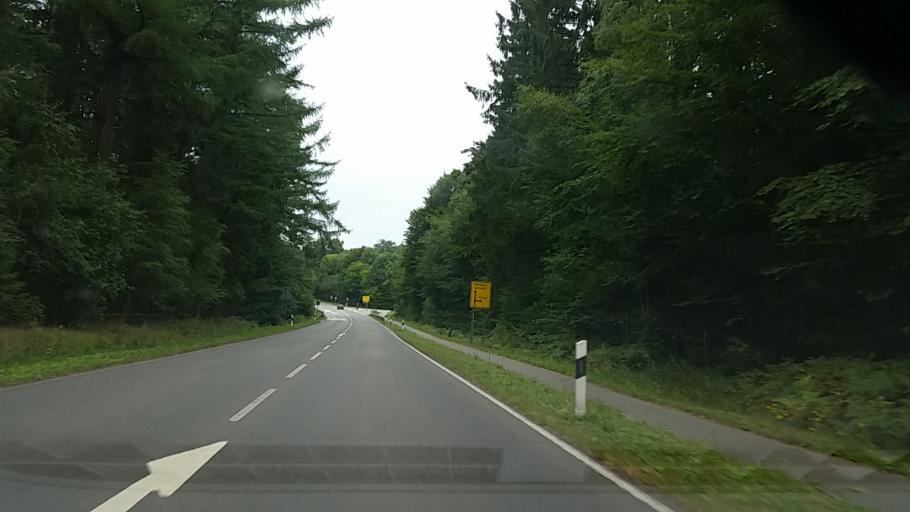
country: DE
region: Schleswig-Holstein
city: Aumuhle
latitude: 53.5216
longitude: 10.3418
